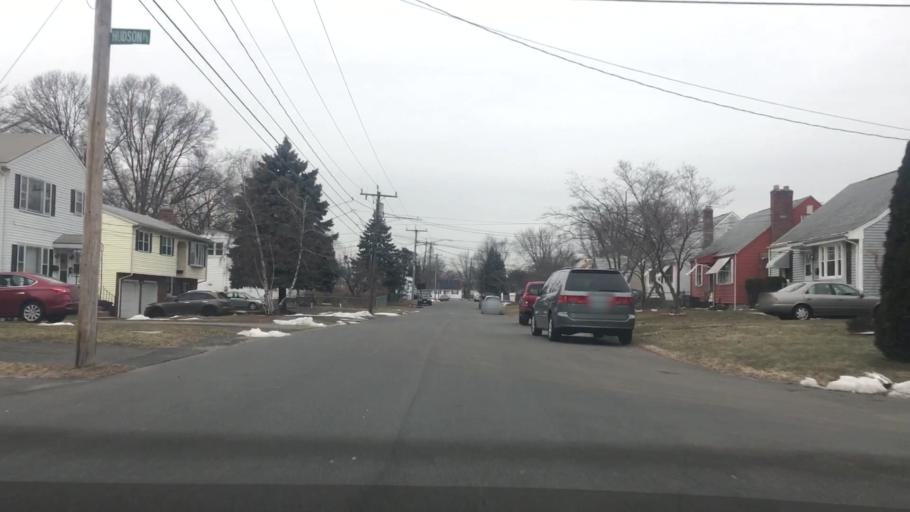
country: US
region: Connecticut
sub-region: Hartford County
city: Kensington
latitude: 41.6515
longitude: -72.7550
